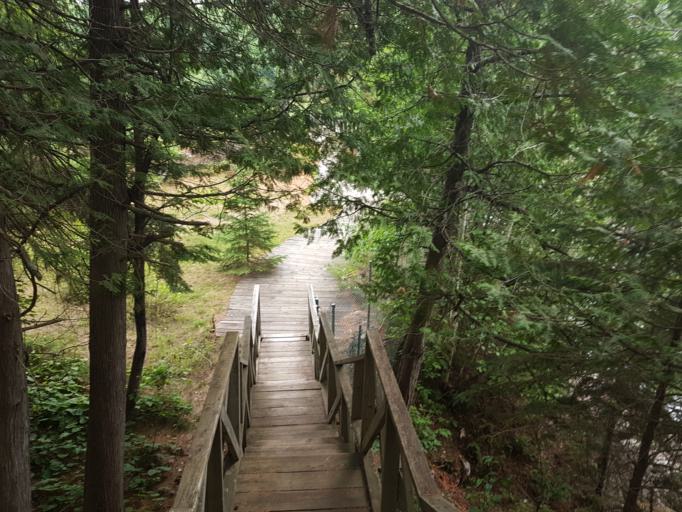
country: CA
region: Quebec
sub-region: Outaouais
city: Fort-Coulonge
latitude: 45.8743
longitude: -76.6859
